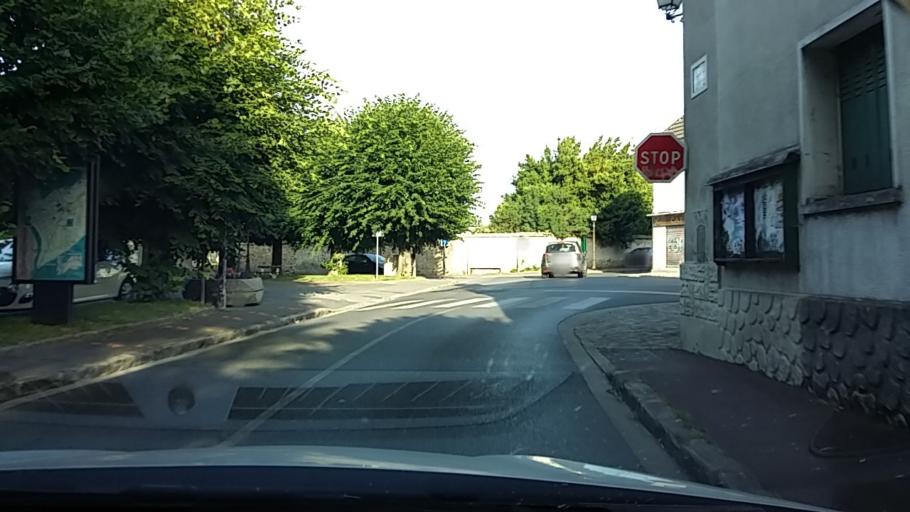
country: FR
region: Ile-de-France
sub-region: Departement du Val-de-Marne
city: Noiseau
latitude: 48.7788
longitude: 2.5479
